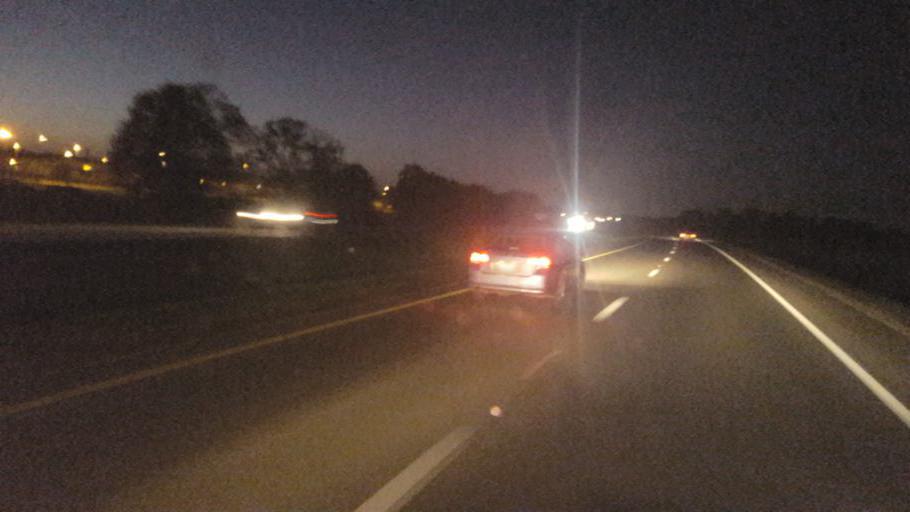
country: US
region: Ohio
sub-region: Pickaway County
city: Circleville
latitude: 39.6129
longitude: -82.9487
